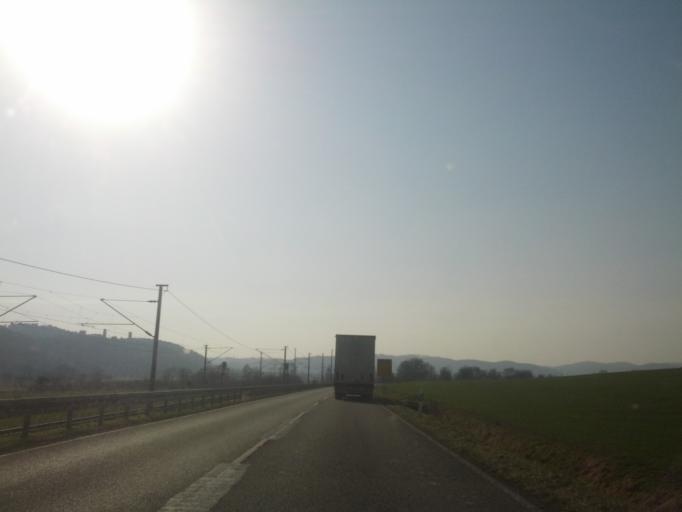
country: DE
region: Hesse
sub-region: Regierungsbezirk Kassel
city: Herleshausen
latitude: 51.0032
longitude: 10.1895
